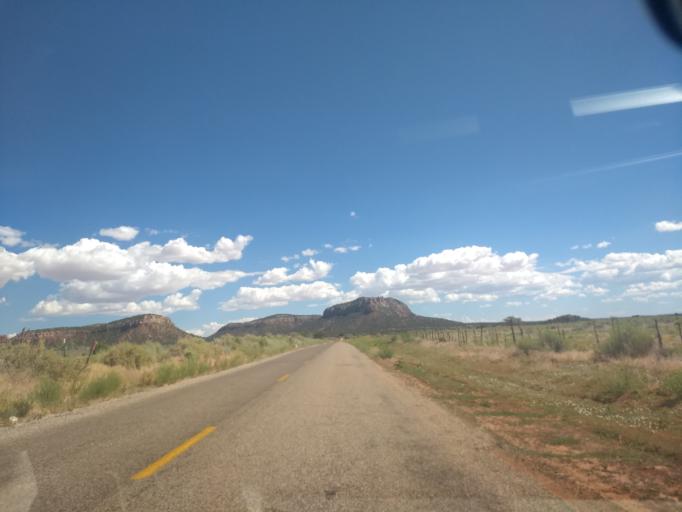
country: US
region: Utah
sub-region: Washington County
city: Hildale
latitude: 36.9508
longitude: -112.8746
